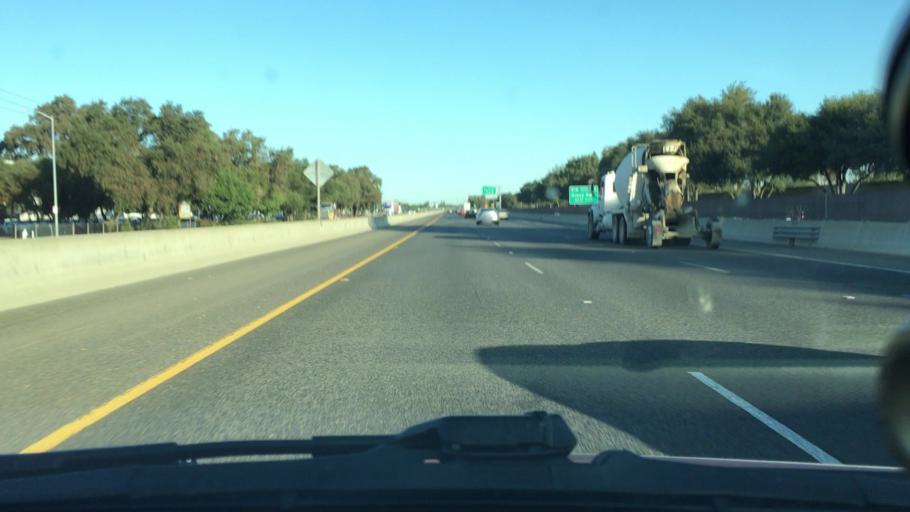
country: US
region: California
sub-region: Sacramento County
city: Elk Grove
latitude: 38.4019
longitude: -121.3839
